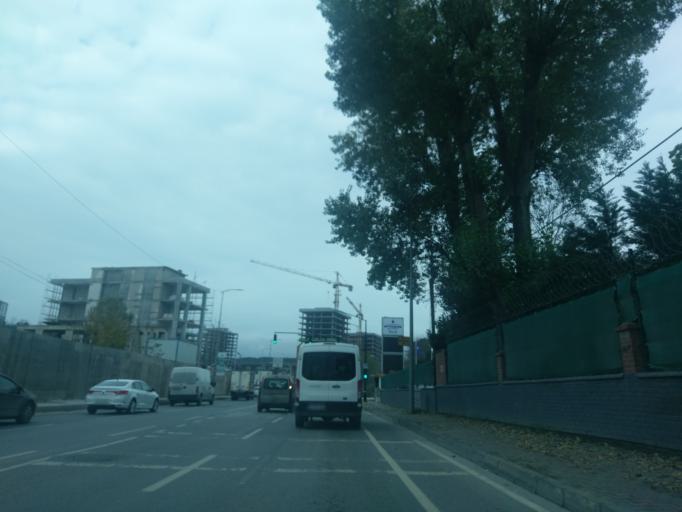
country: TR
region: Istanbul
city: Sisli
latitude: 41.0951
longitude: 28.9831
